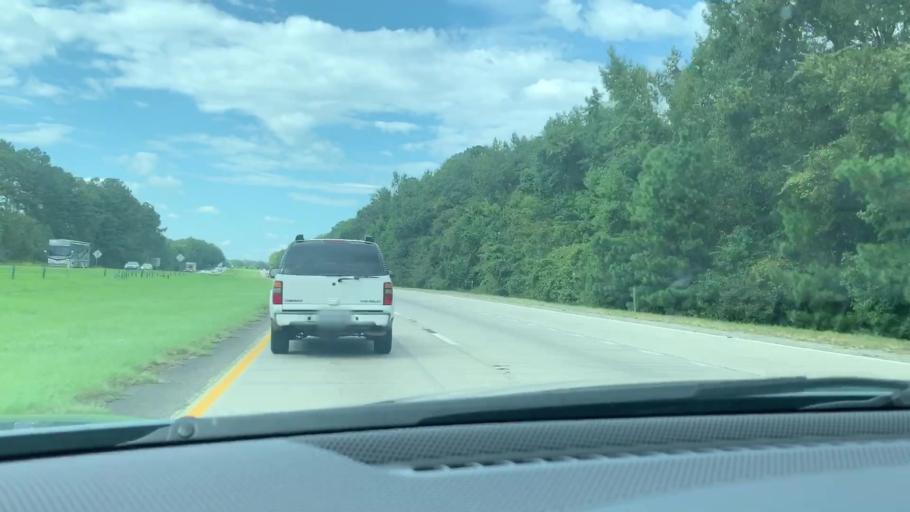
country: US
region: South Carolina
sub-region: Hampton County
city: Yemassee
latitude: 32.6366
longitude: -80.8816
